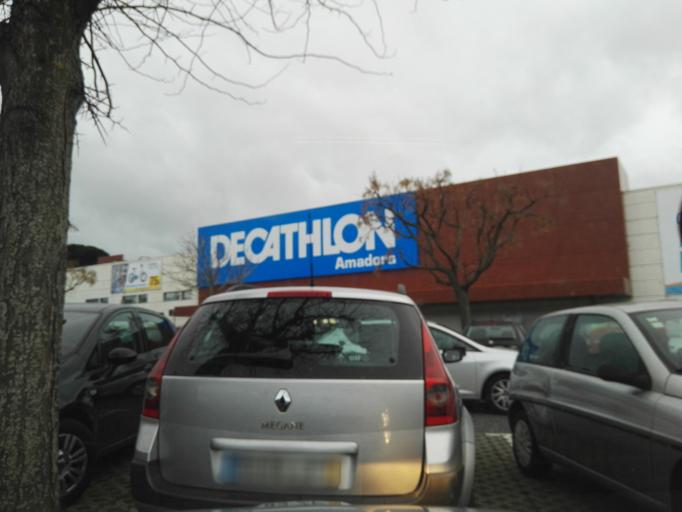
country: PT
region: Lisbon
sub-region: Cascais
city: Sao Domingos de Rana
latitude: 38.7118
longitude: -9.3402
